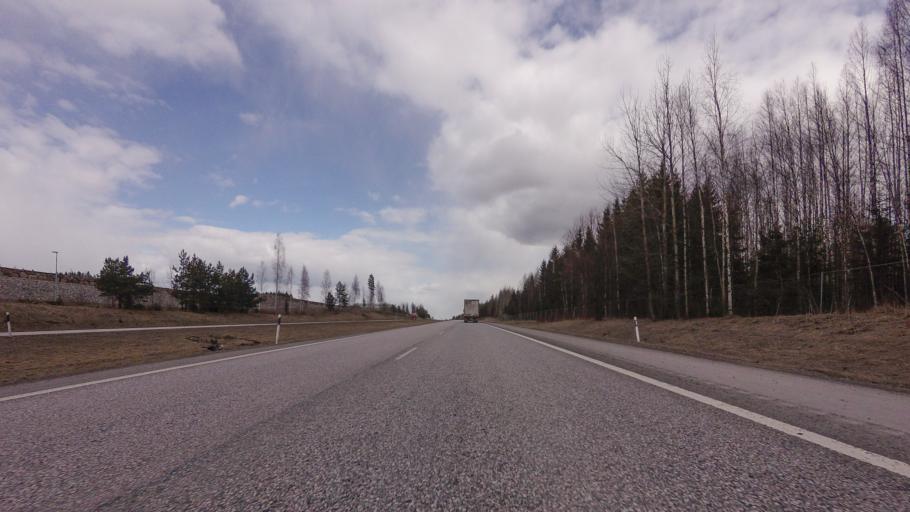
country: FI
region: Uusimaa
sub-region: Helsinki
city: Nurmijaervi
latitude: 60.4389
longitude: 24.8356
